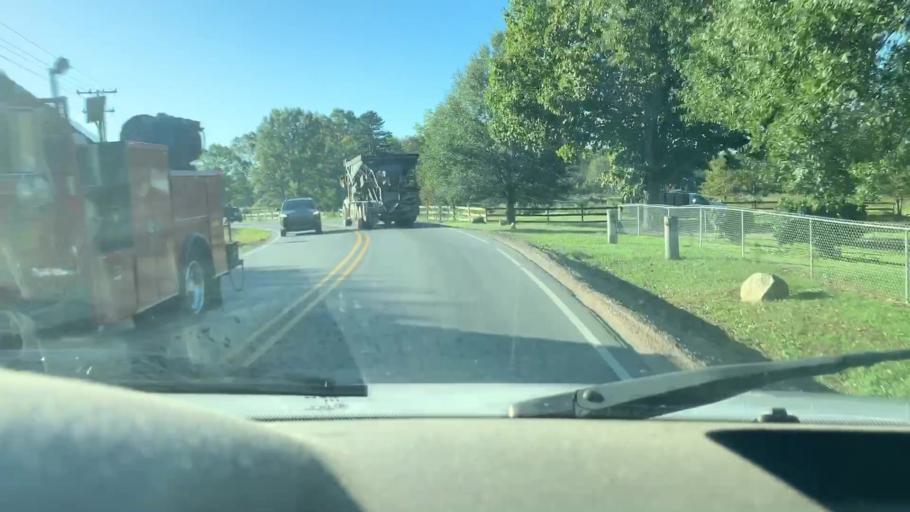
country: US
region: North Carolina
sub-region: Mecklenburg County
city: Huntersville
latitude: 35.4327
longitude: -80.7627
